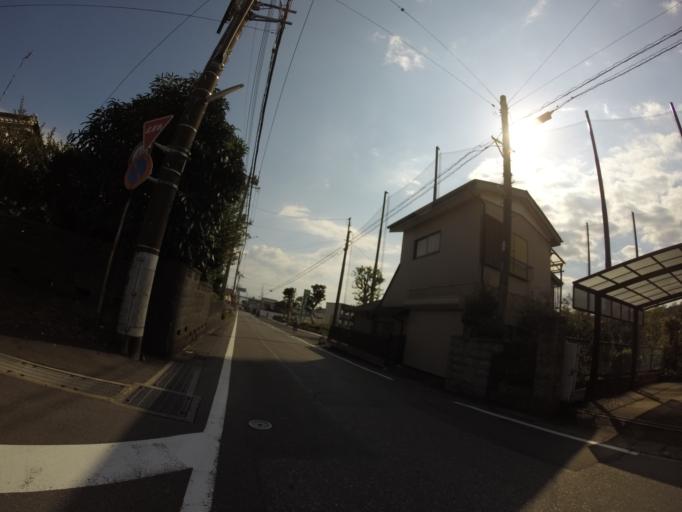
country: JP
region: Shizuoka
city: Fujinomiya
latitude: 35.2065
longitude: 138.6332
